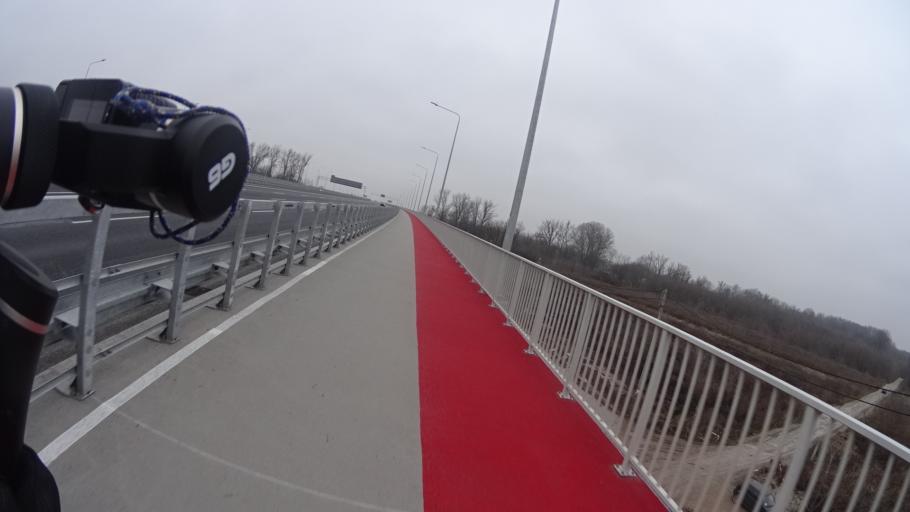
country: PL
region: Masovian Voivodeship
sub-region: Warszawa
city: Wawer
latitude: 52.1634
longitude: 21.1534
